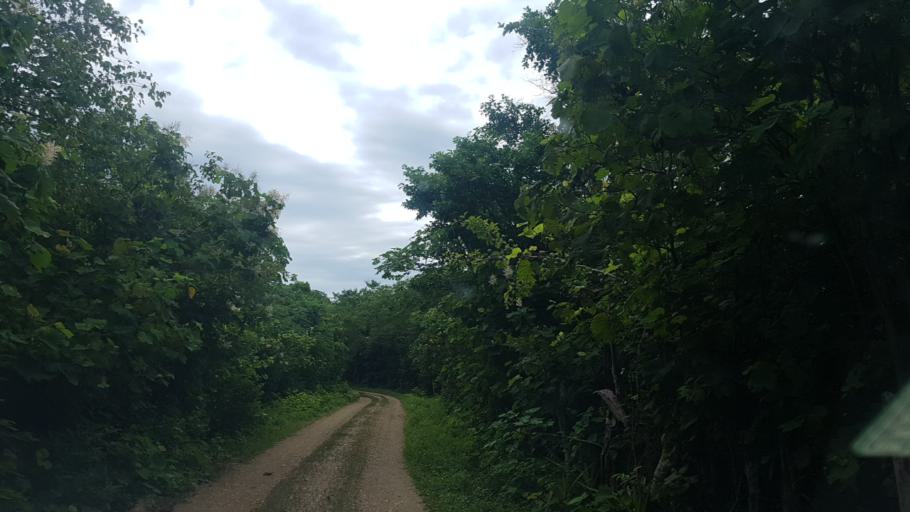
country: NI
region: Nueva Segovia
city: Ciudad Antigua
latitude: 13.6005
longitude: -86.3618
